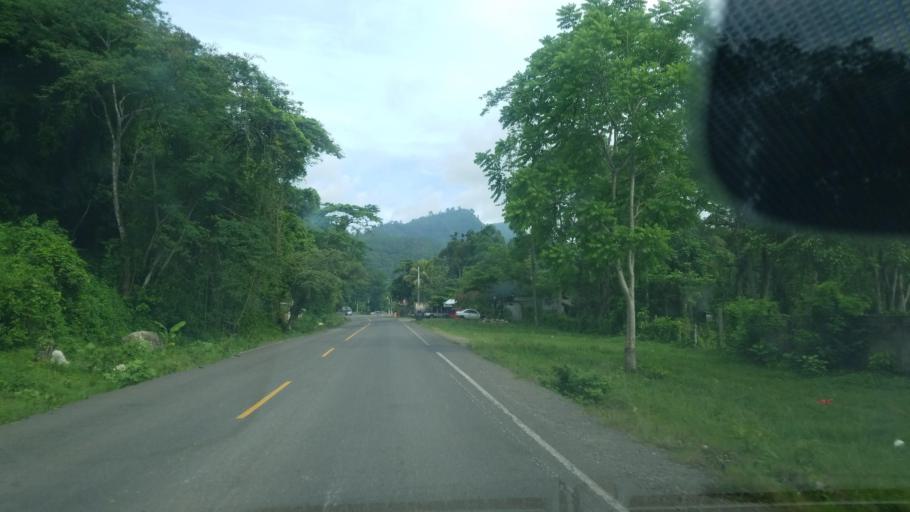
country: HN
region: Santa Barbara
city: Petoa
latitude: 15.2481
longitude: -88.2725
